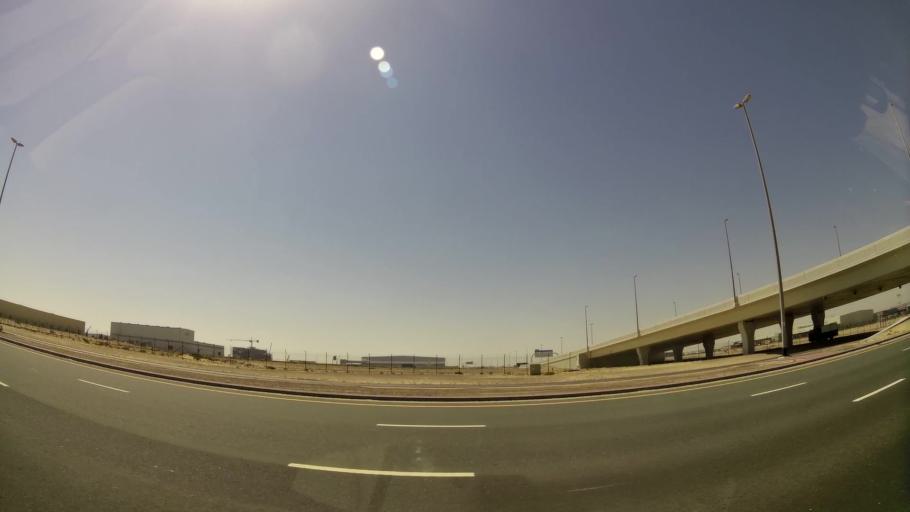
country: AE
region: Dubai
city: Dubai
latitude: 24.9352
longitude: 55.0986
